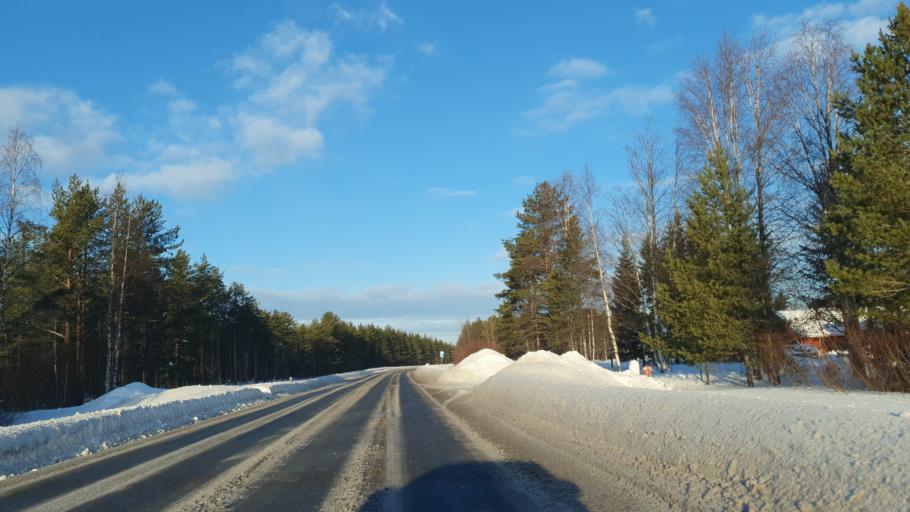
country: FI
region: Northern Ostrobothnia
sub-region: Oulunkaari
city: Utajaervi
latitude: 64.7260
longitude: 26.4932
